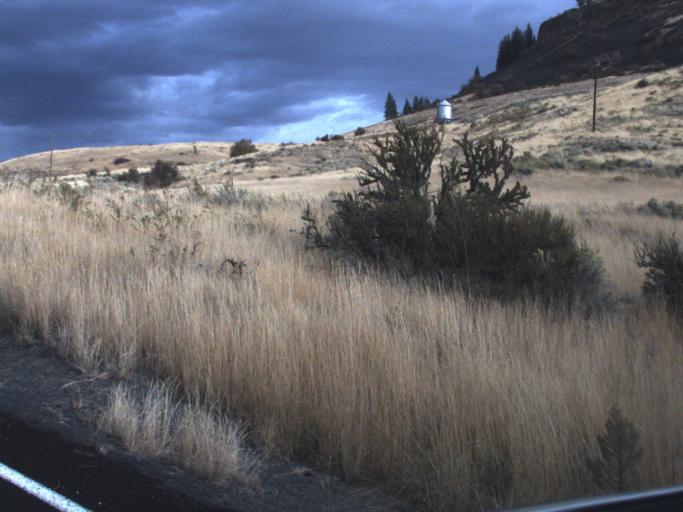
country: US
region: Washington
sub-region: Okanogan County
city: Coulee Dam
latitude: 47.9055
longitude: -118.6948
